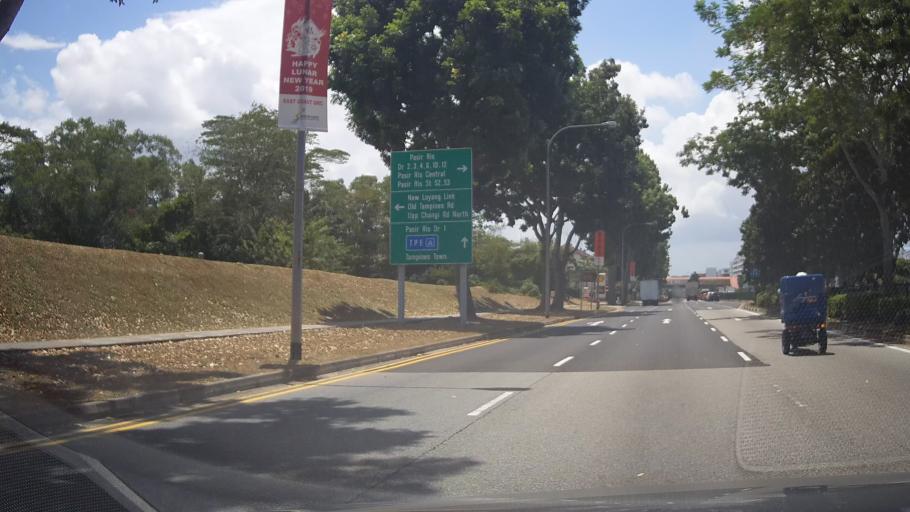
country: MY
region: Johor
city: Kampung Pasir Gudang Baru
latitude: 1.3671
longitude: 103.9680
